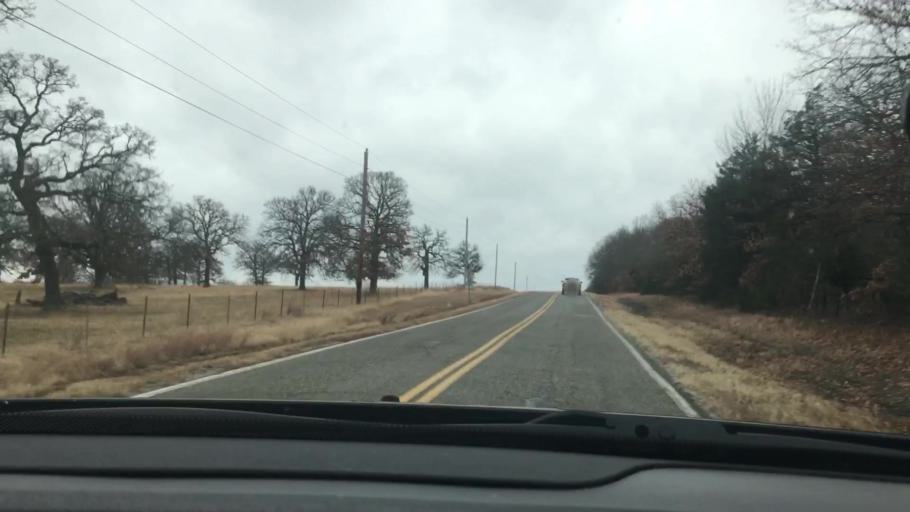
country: US
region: Oklahoma
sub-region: Johnston County
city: Tishomingo
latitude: 34.1963
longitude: -96.5776
